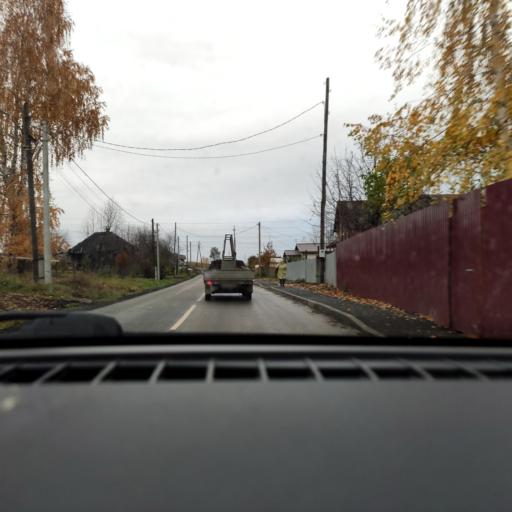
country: RU
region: Perm
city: Ferma
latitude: 57.9194
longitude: 56.3022
